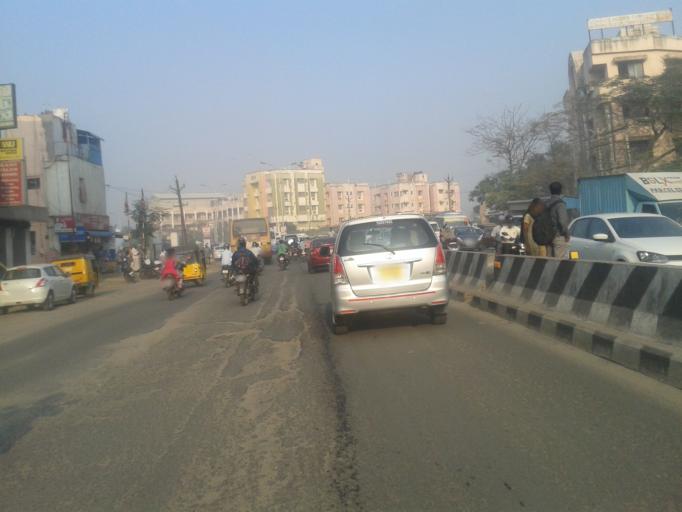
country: IN
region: Tamil Nadu
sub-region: Thiruvallur
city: Porur
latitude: 13.0360
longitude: 80.1535
